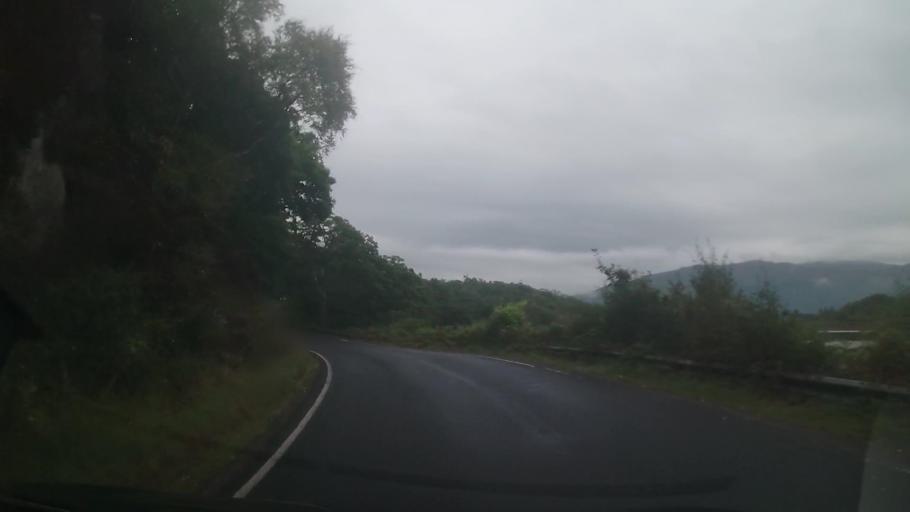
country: GB
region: Scotland
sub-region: Argyll and Bute
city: Isle Of Mull
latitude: 56.6991
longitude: -5.6925
